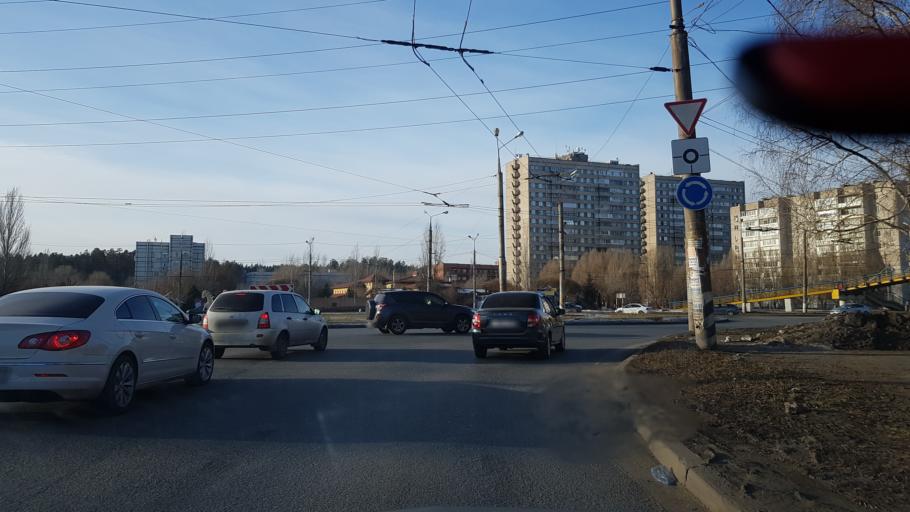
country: RU
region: Samara
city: Tol'yatti
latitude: 53.5293
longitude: 49.3976
